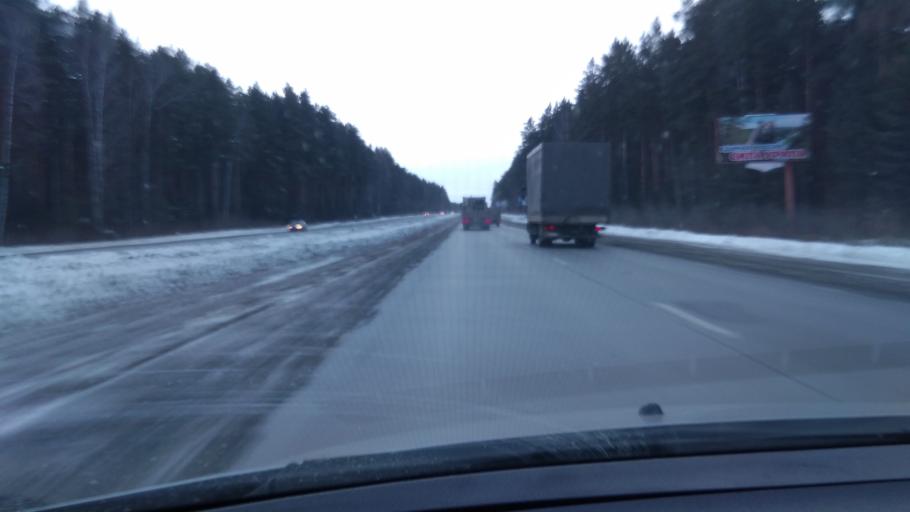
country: RU
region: Sverdlovsk
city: Sysert'
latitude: 56.5741
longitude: 60.8592
